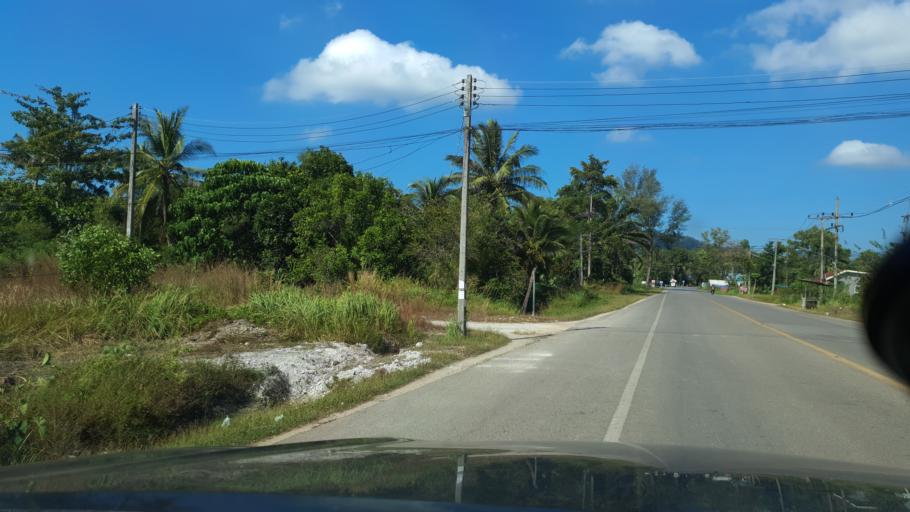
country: TH
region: Krabi
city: Krabi
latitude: 8.0271
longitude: 98.8740
